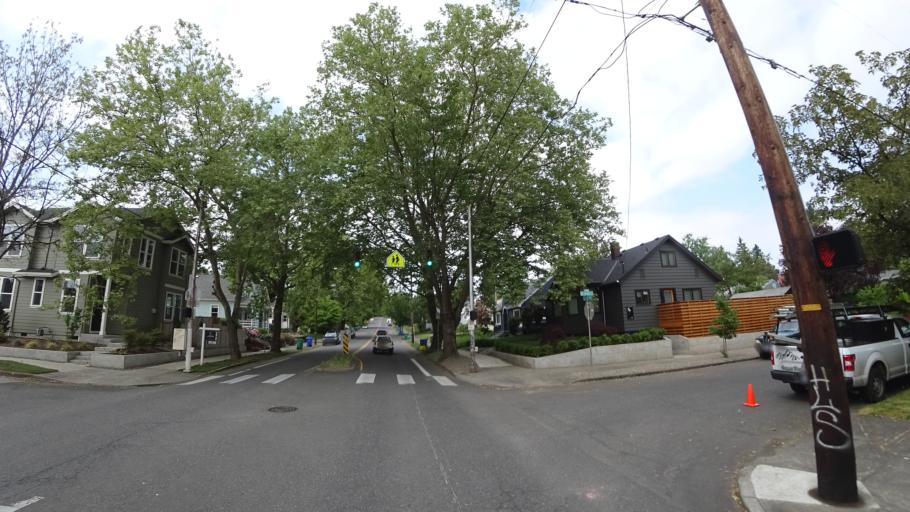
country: US
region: Oregon
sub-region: Multnomah County
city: Portland
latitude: 45.5517
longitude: -122.6504
